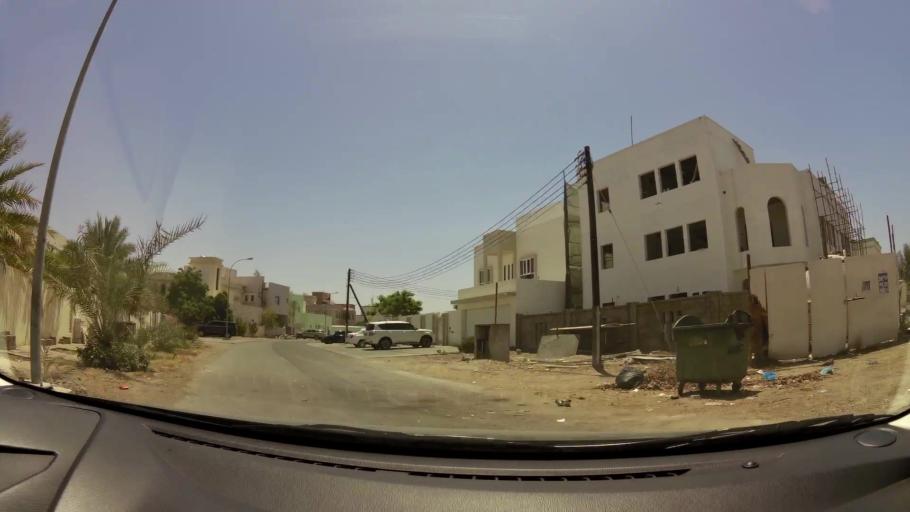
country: OM
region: Muhafazat Masqat
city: As Sib al Jadidah
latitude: 23.6145
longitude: 58.2307
